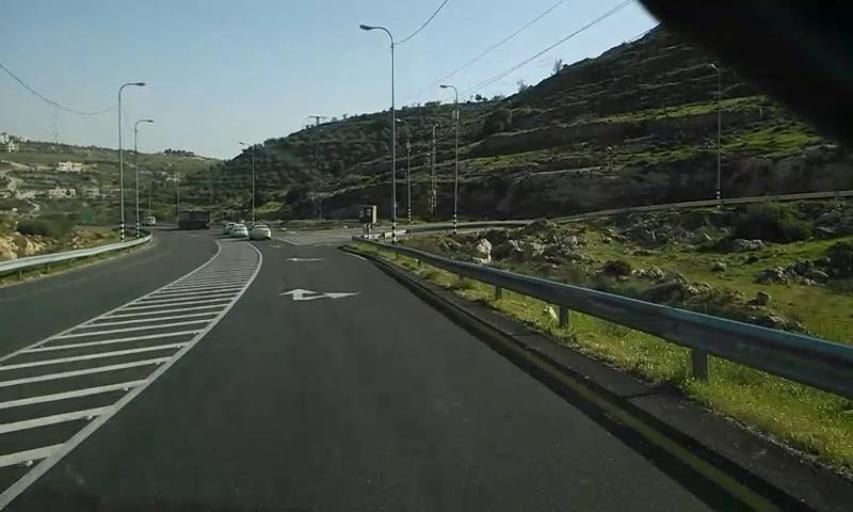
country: PS
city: Al Buq`ah
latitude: 31.5184
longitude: 35.1336
